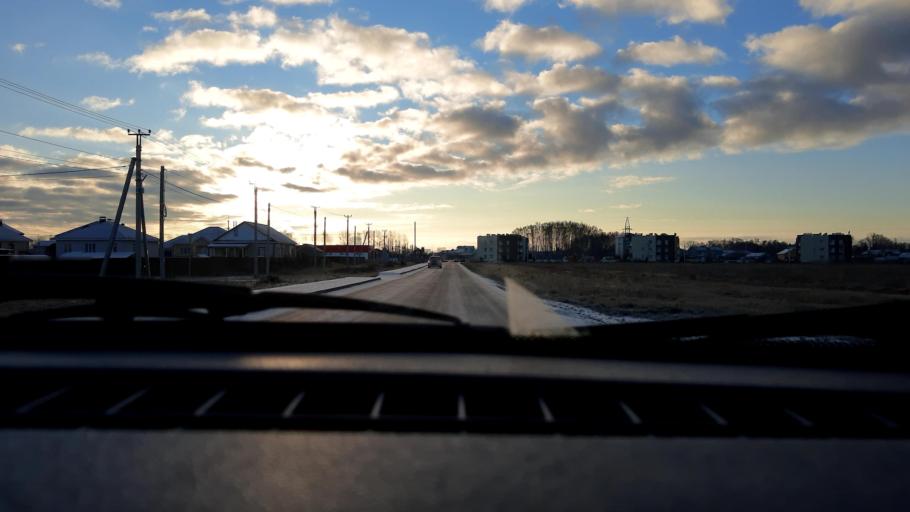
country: RU
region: Bashkortostan
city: Mikhaylovka
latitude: 54.7862
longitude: 55.8309
